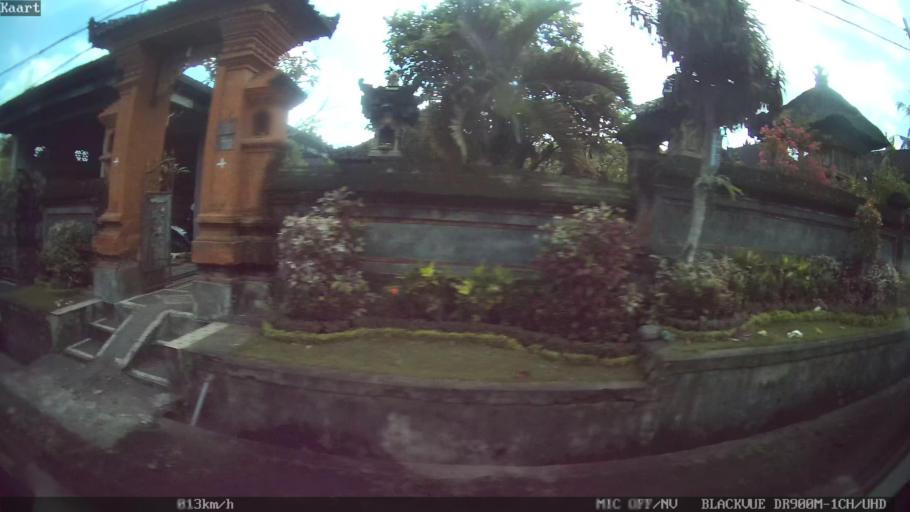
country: ID
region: Bali
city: Banjar Pesalakan
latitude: -8.5156
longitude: 115.3061
